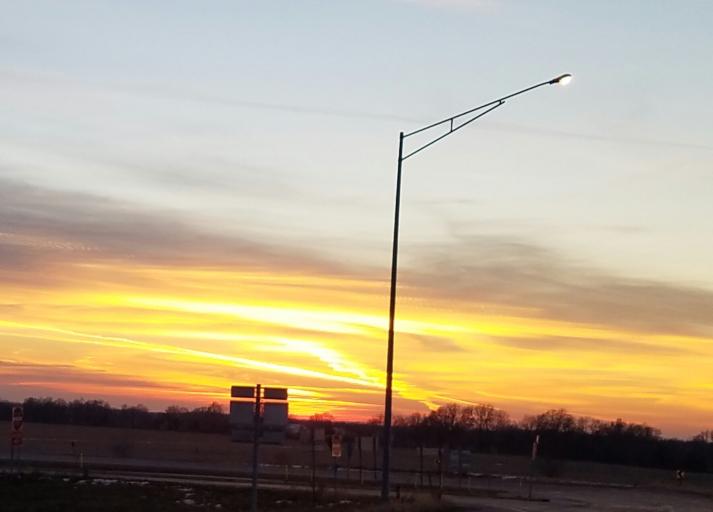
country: US
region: Missouri
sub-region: Boone County
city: Hallsville
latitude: 39.2462
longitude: -92.3245
